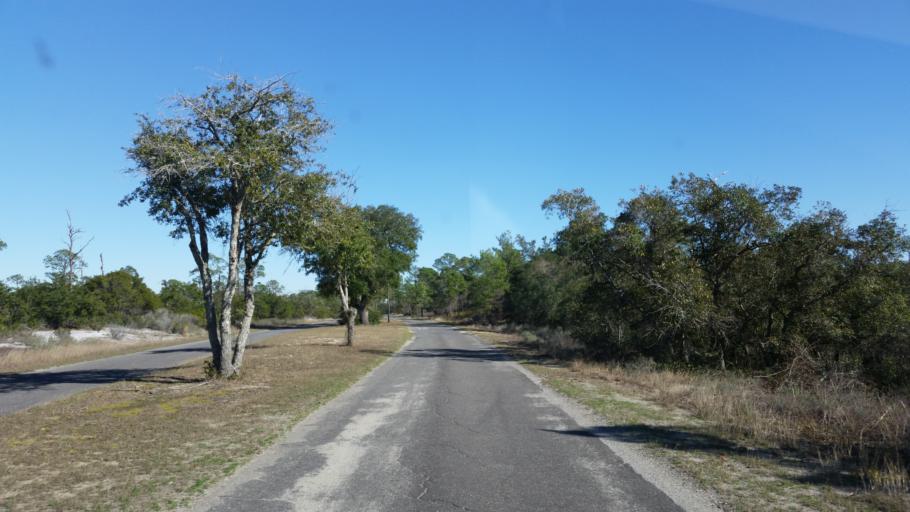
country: US
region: Florida
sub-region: Escambia County
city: Myrtle Grove
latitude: 30.3162
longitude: -87.4076
